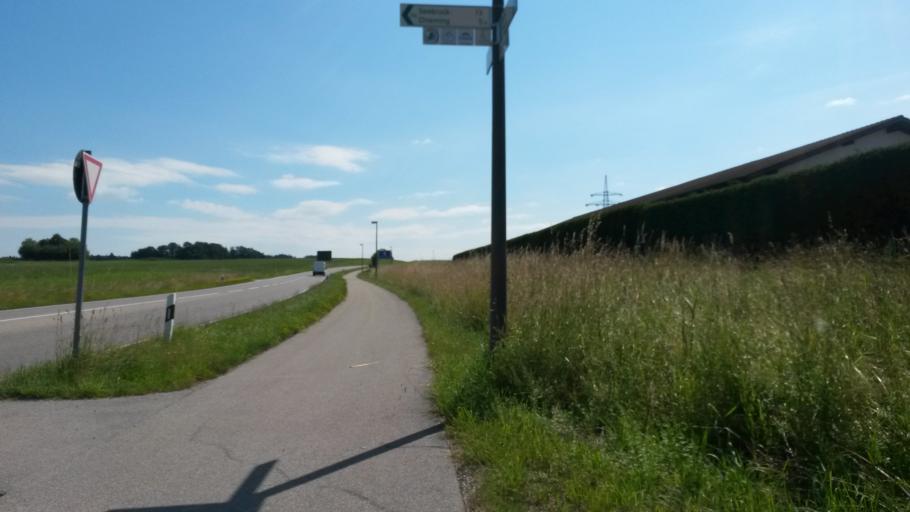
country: DE
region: Bavaria
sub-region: Upper Bavaria
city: Grabenstatt
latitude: 47.8511
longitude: 12.5417
